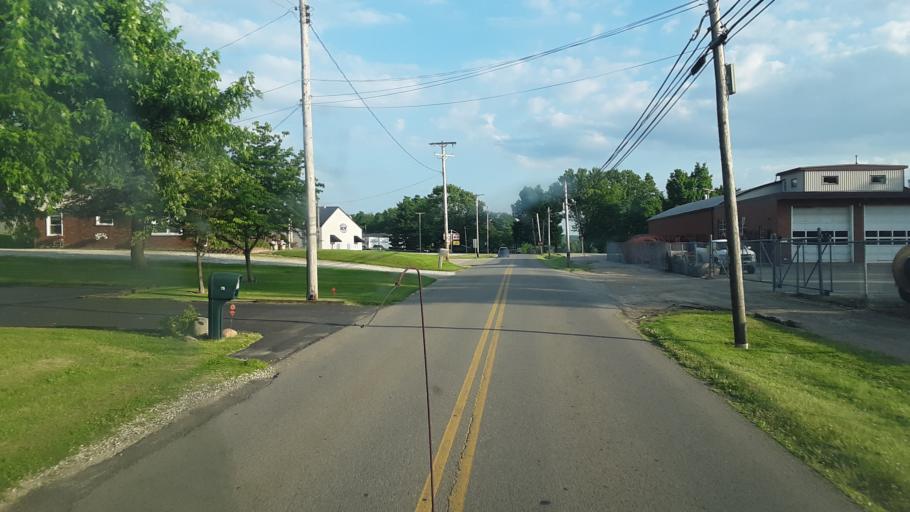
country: US
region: Ohio
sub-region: Richland County
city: Lincoln Heights
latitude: 40.7561
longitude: -82.4749
